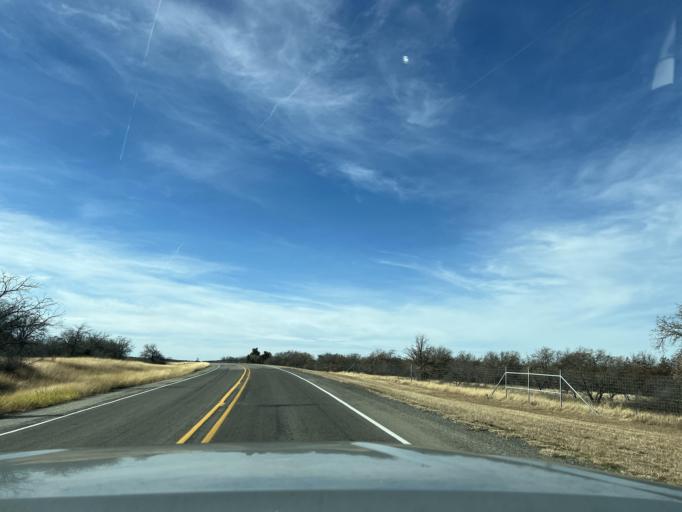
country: US
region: Texas
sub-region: Eastland County
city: Cisco
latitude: 32.4591
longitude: -98.9931
